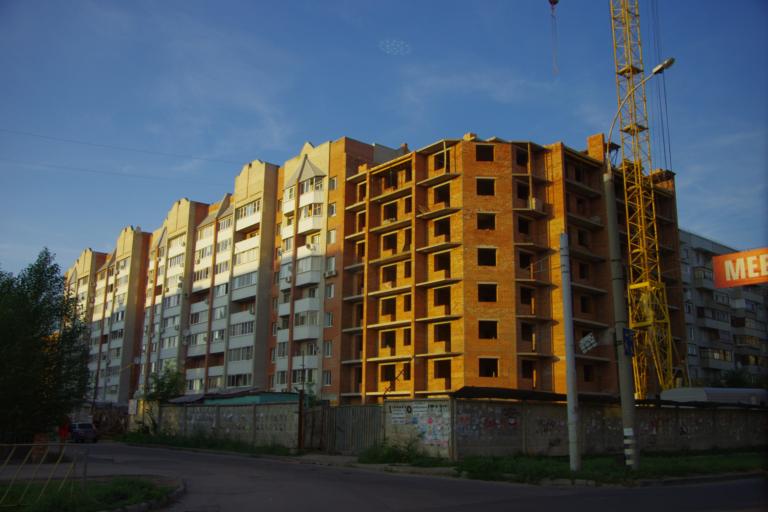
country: RU
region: Samara
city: Tol'yatti
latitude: 53.5327
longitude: 49.3354
